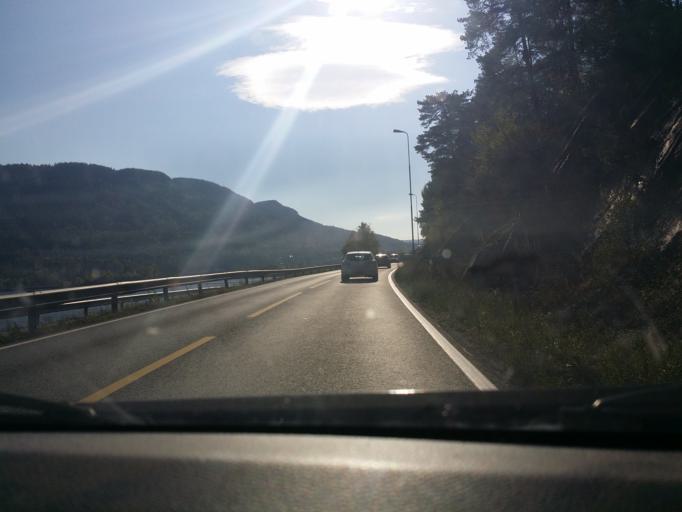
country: NO
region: Buskerud
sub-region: Hole
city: Vik
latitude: 60.0700
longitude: 10.3015
